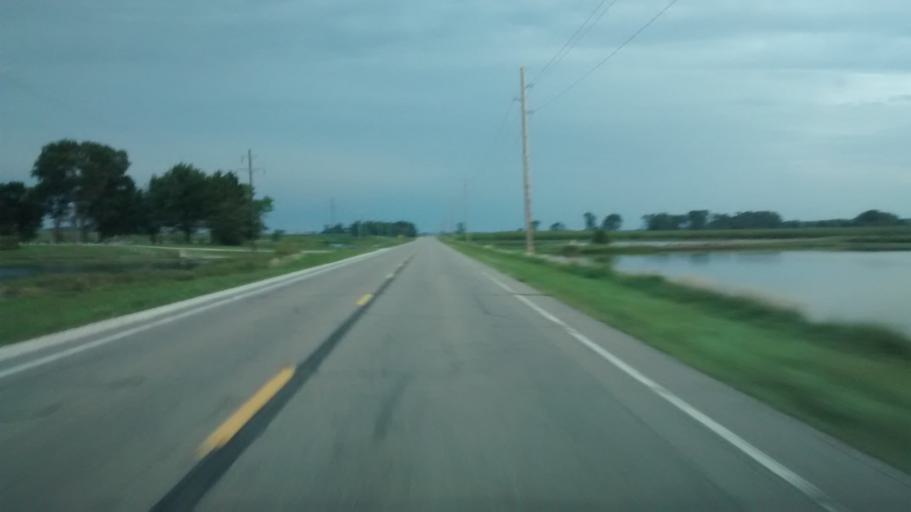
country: US
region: Iowa
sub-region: Woodbury County
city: Moville
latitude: 42.5412
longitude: -96.0282
